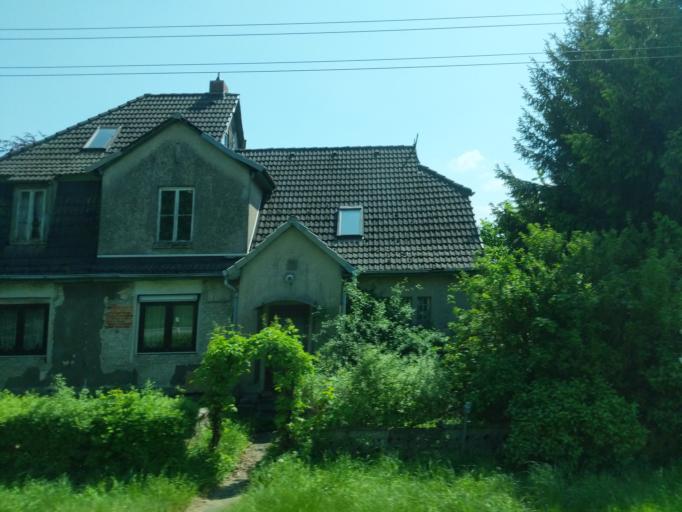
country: DE
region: Mecklenburg-Vorpommern
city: Stralendorf
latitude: 53.5563
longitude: 11.3359
